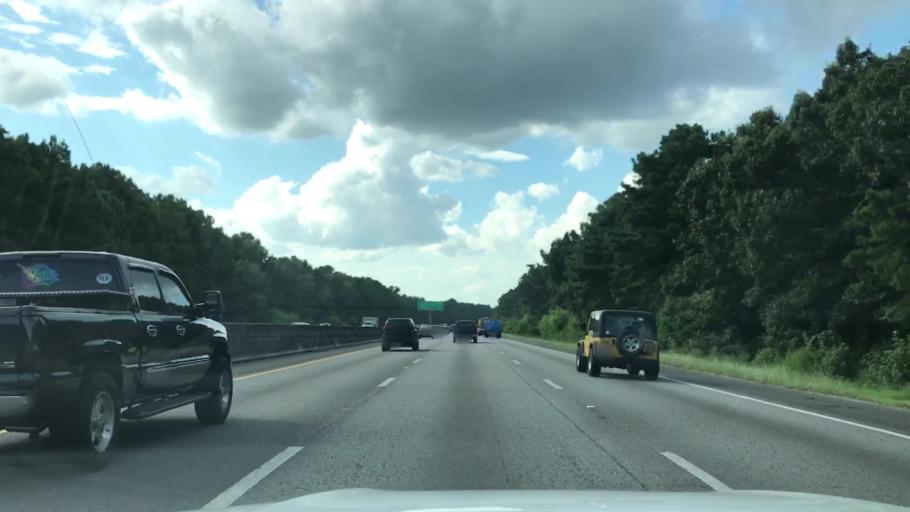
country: US
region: South Carolina
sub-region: Berkeley County
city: Goose Creek
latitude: 32.9571
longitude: -80.0674
